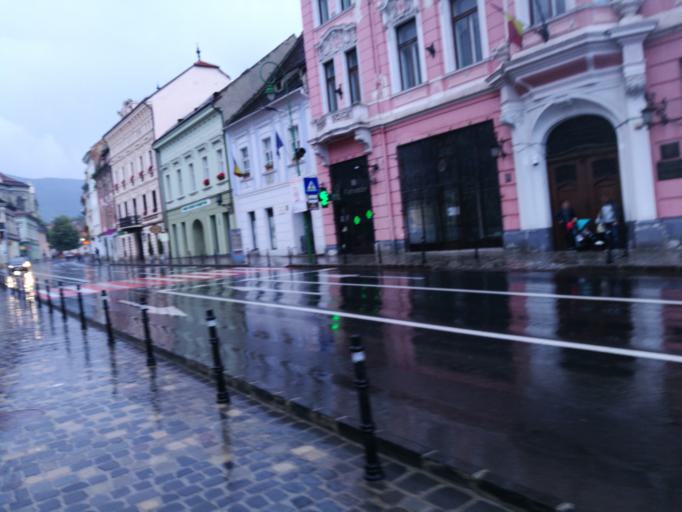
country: RO
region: Brasov
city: Brasov
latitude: 45.6426
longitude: 25.5887
